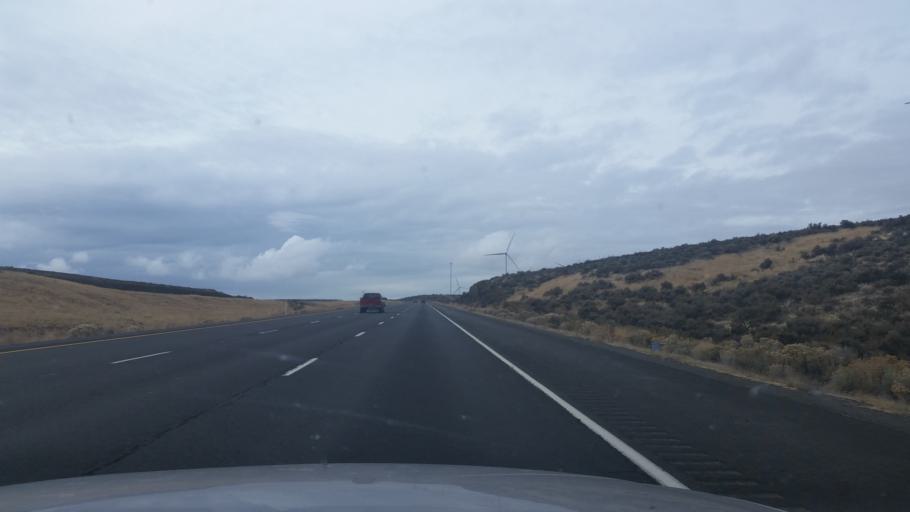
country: US
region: Washington
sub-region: Kittitas County
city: Kittitas
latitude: 46.9444
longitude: -120.1840
